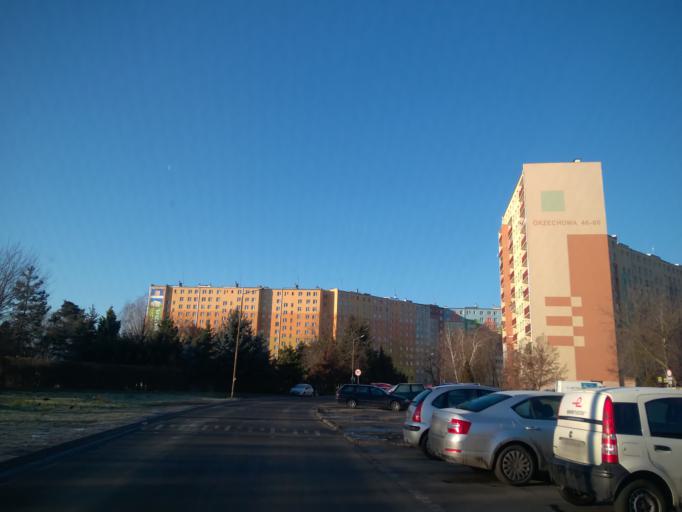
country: PL
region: Lower Silesian Voivodeship
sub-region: Powiat wroclawski
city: Wroclaw
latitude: 51.0785
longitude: 17.0434
